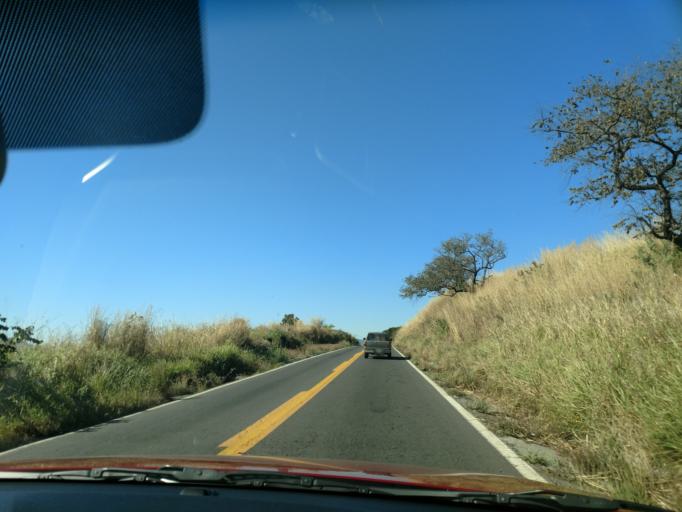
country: MX
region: Nayarit
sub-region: Ahuacatlan
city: Ahuacatlan
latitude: 21.1187
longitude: -104.5923
